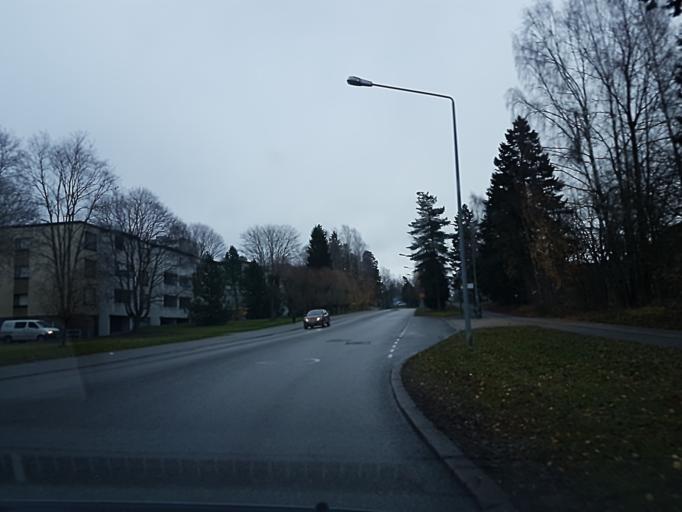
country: FI
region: Uusimaa
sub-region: Helsinki
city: Vantaa
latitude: 60.2376
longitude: 25.1116
